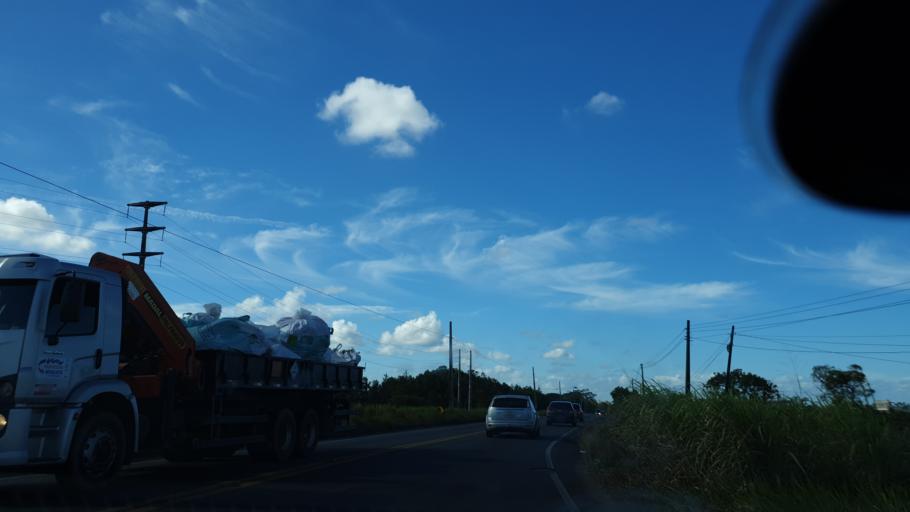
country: BR
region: Bahia
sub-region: Camacari
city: Camacari
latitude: -12.6663
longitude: -38.3009
